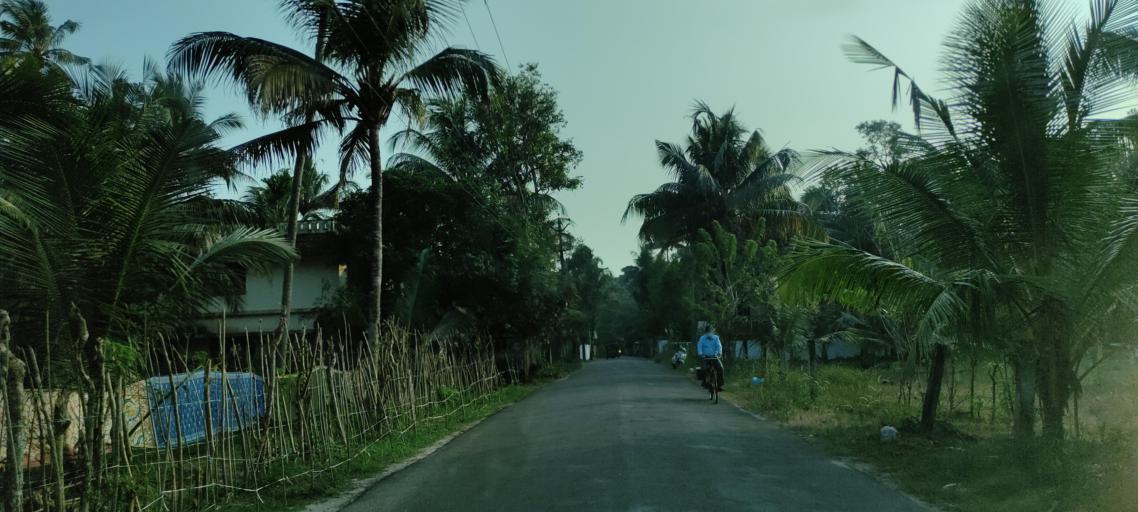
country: IN
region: Kerala
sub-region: Alappuzha
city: Shertallai
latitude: 9.6649
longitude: 76.3535
